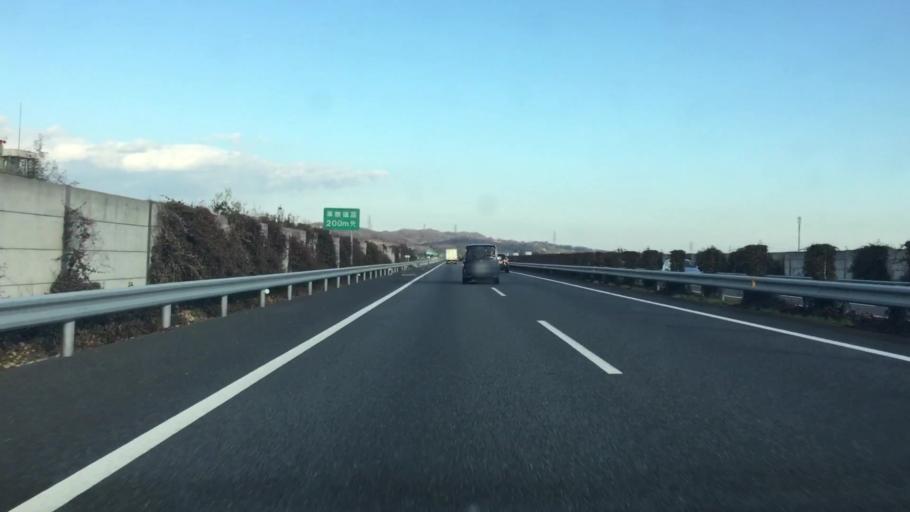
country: JP
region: Gunma
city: Kiryu
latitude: 36.3461
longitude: 139.3032
